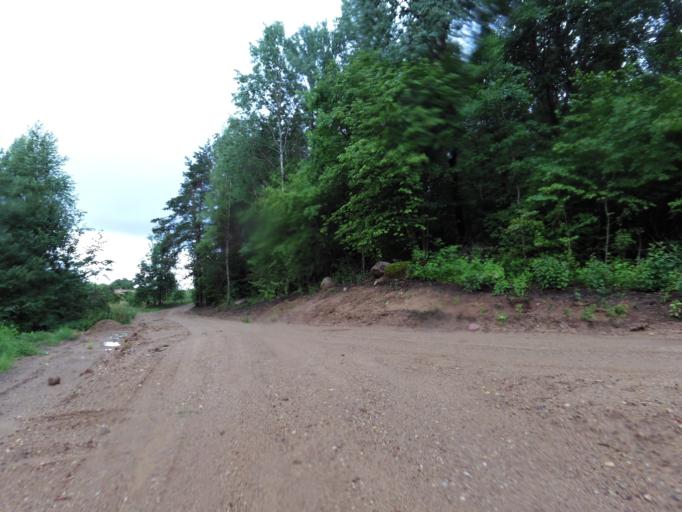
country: LT
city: Grigiskes
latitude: 54.7148
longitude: 25.1122
